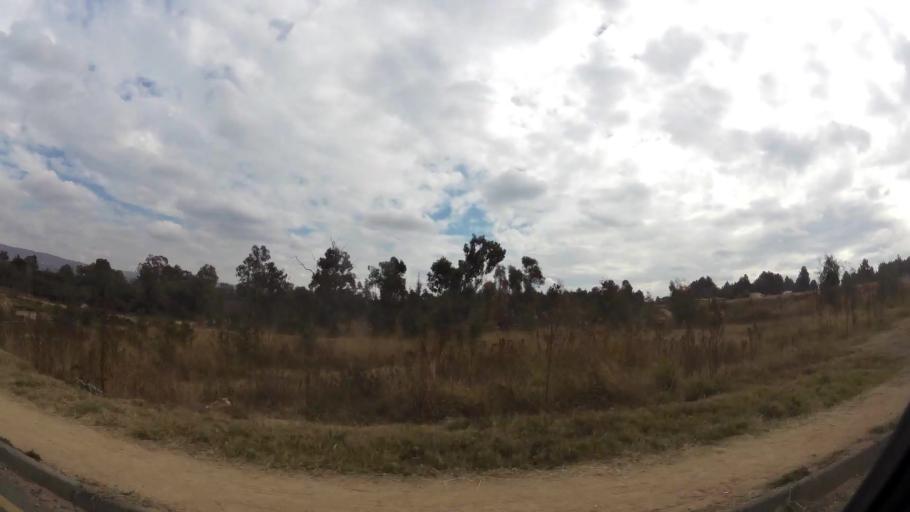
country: ZA
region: Gauteng
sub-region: West Rand District Municipality
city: Muldersdriseloop
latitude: -26.0656
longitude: 27.8954
